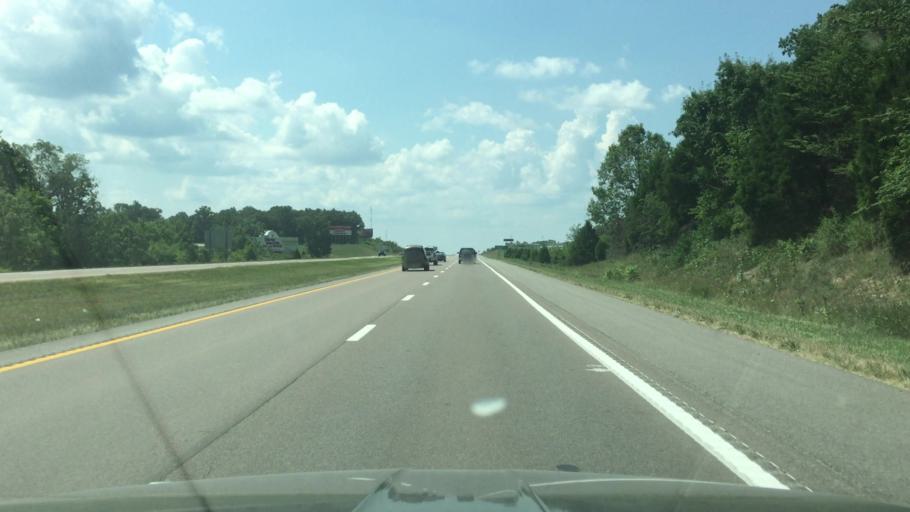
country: US
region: Missouri
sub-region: Miller County
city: Eldon
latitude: 38.2991
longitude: -92.5800
